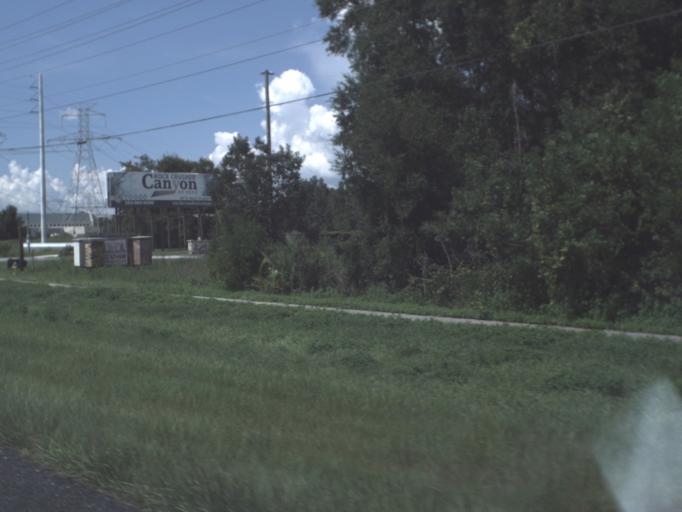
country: US
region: Florida
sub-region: Citrus County
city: Lecanto
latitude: 28.8559
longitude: -82.5002
